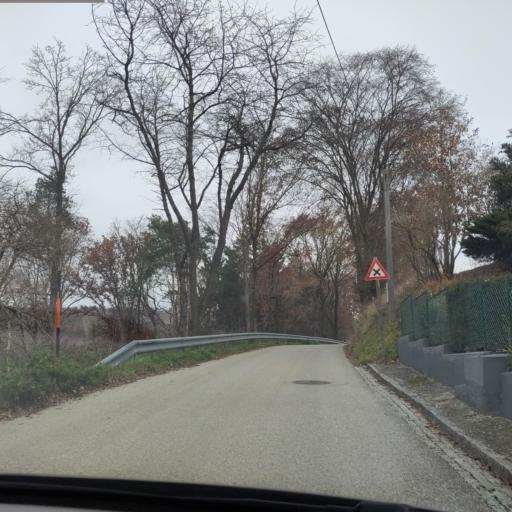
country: AT
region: Lower Austria
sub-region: Politischer Bezirk Sankt Polten
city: Neidling
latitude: 48.2450
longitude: 15.5518
